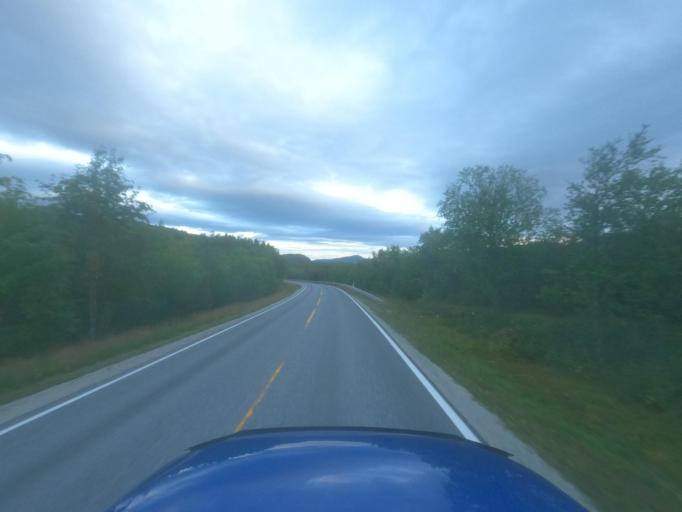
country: NO
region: Finnmark Fylke
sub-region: Porsanger
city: Lakselv
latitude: 69.9459
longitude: 24.9589
